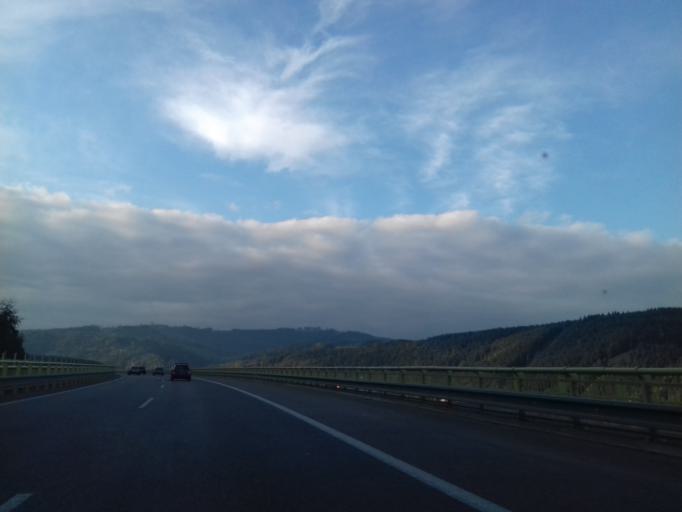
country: SK
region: Zilinsky
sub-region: Okres Zilina
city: Zilina
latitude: 49.2502
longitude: 18.6847
